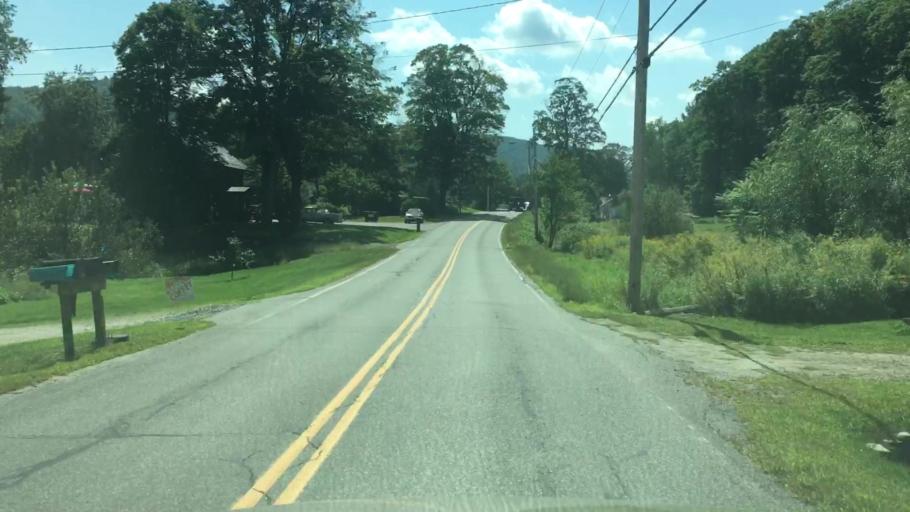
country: US
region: Vermont
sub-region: Windham County
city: West Brattleboro
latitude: 42.7959
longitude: -72.5987
